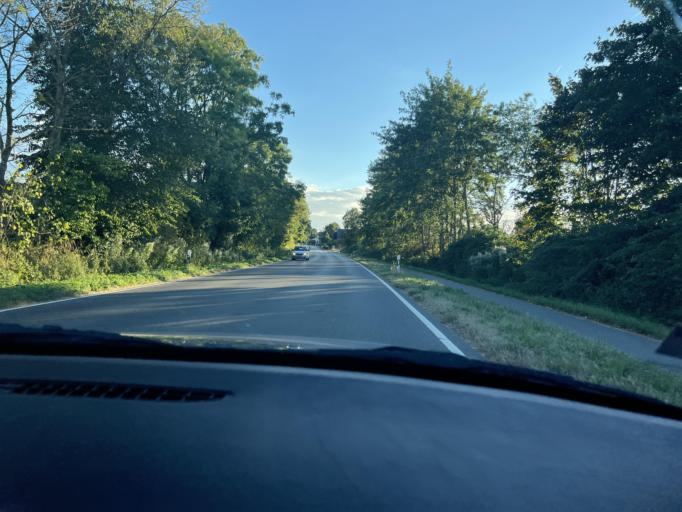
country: DE
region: Schleswig-Holstein
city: Norderheistedt
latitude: 54.2371
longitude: 9.1525
